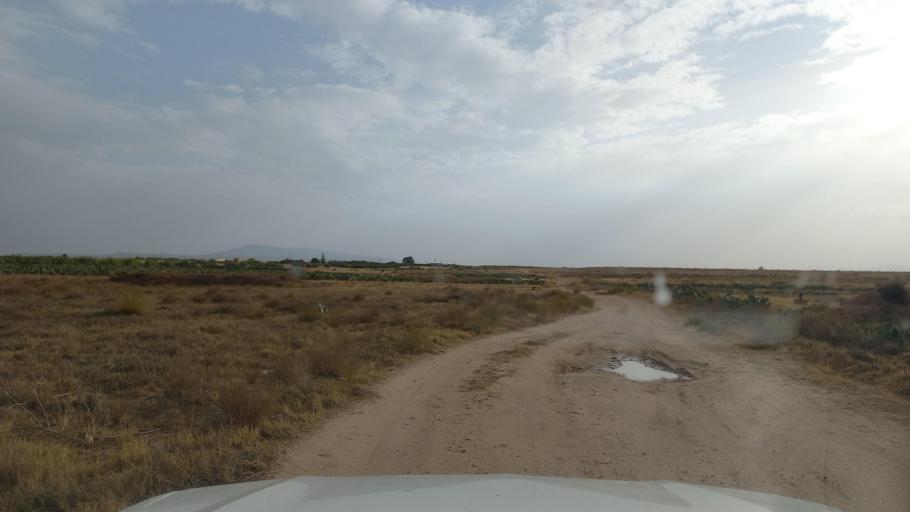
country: TN
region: Al Qasrayn
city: Kasserine
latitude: 35.2906
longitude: 9.0482
